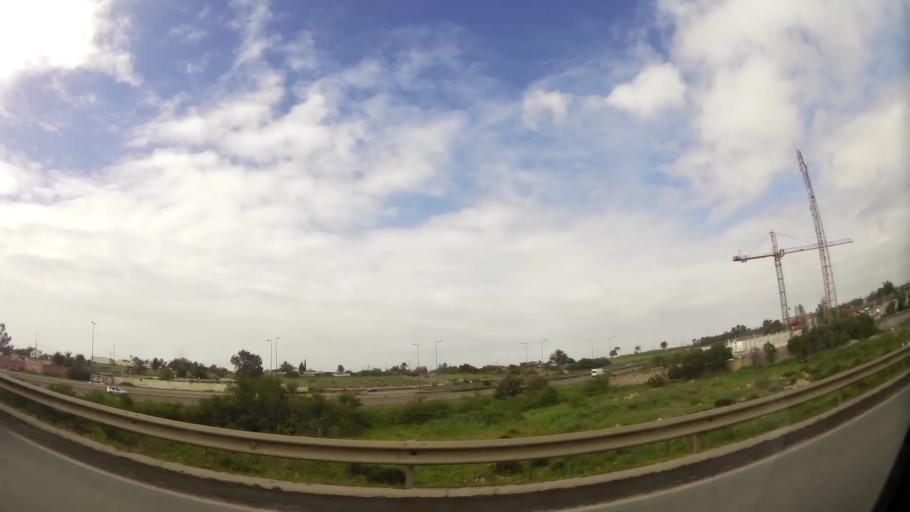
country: MA
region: Grand Casablanca
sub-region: Mohammedia
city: Mohammedia
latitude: 33.6405
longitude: -7.4331
